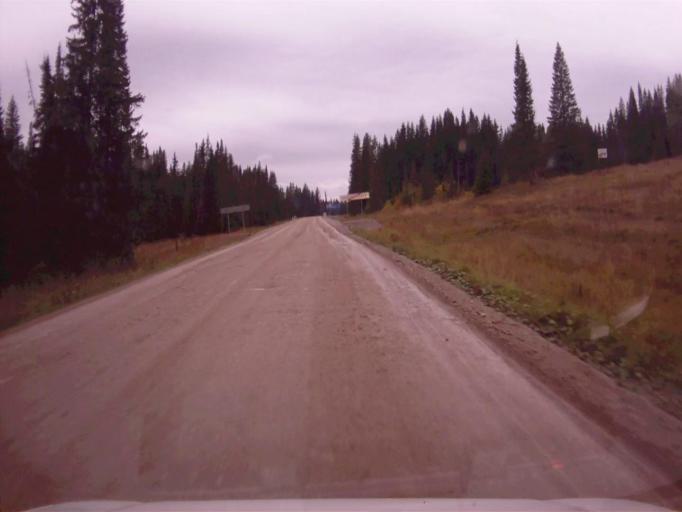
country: RU
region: Chelyabinsk
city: Nyazepetrovsk
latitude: 56.0582
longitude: 59.5573
